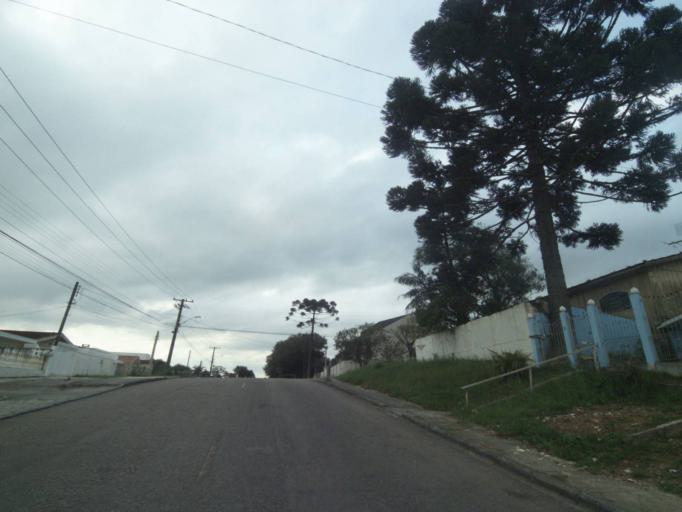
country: BR
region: Parana
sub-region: Pinhais
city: Pinhais
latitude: -25.4153
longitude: -49.2154
